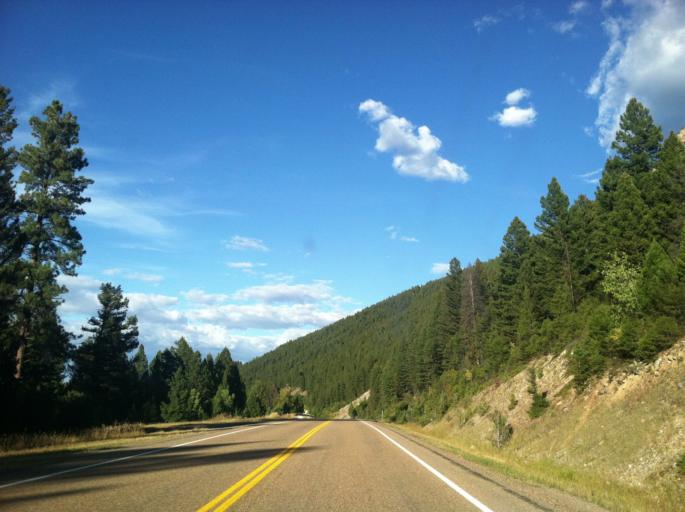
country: US
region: Montana
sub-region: Granite County
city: Philipsburg
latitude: 46.4505
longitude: -113.2445
